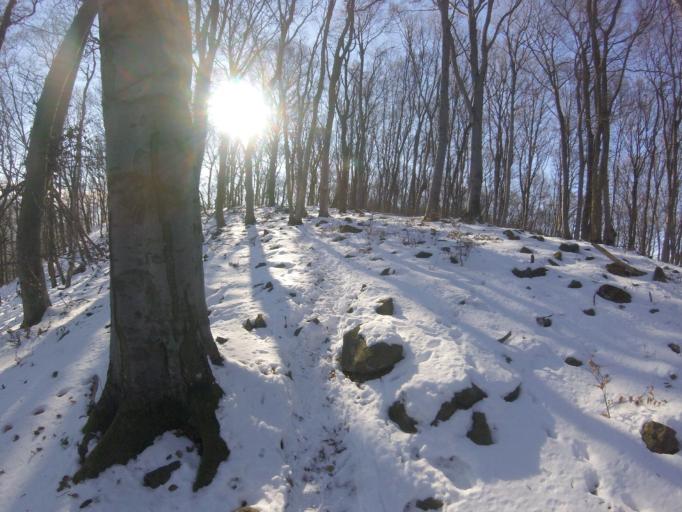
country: SK
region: Nitriansky
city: Sahy
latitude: 47.9758
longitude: 18.8860
